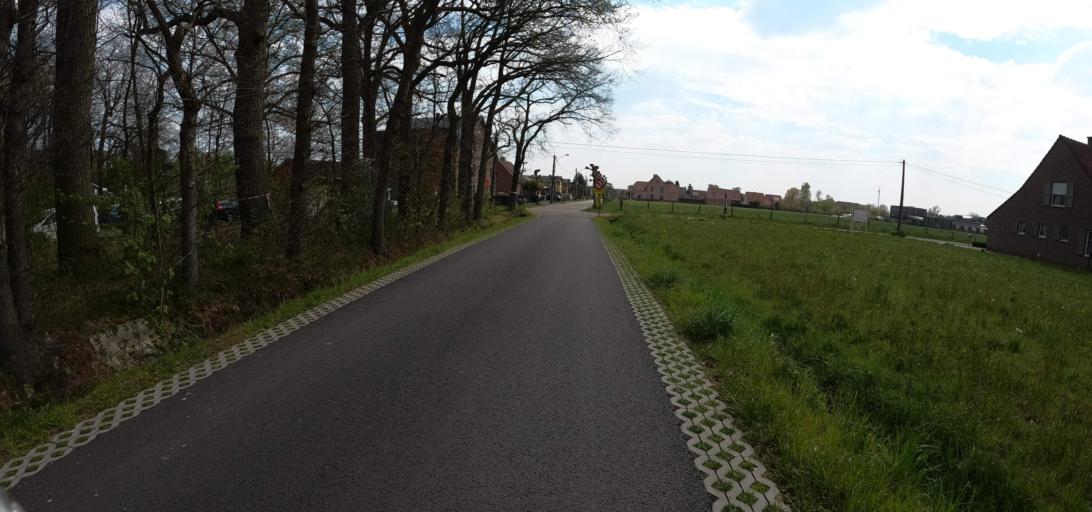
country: BE
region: Flanders
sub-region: Provincie Antwerpen
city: Oostmalle
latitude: 51.3045
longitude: 4.7476
